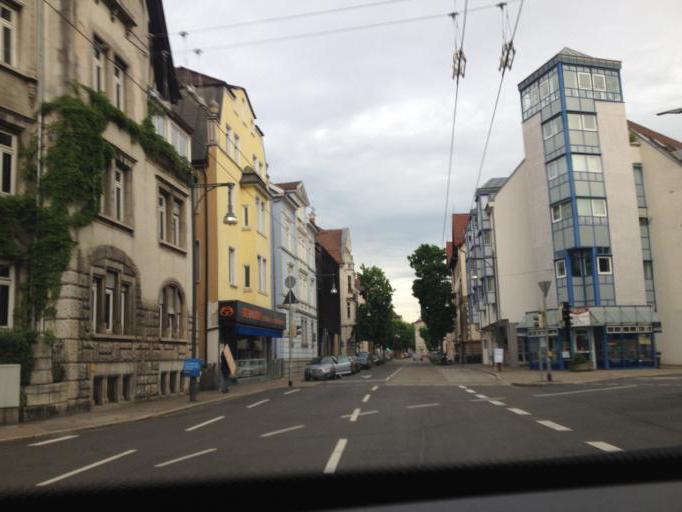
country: DE
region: Baden-Wuerttemberg
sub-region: Regierungsbezirk Stuttgart
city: Esslingen
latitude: 48.7369
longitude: 9.3117
